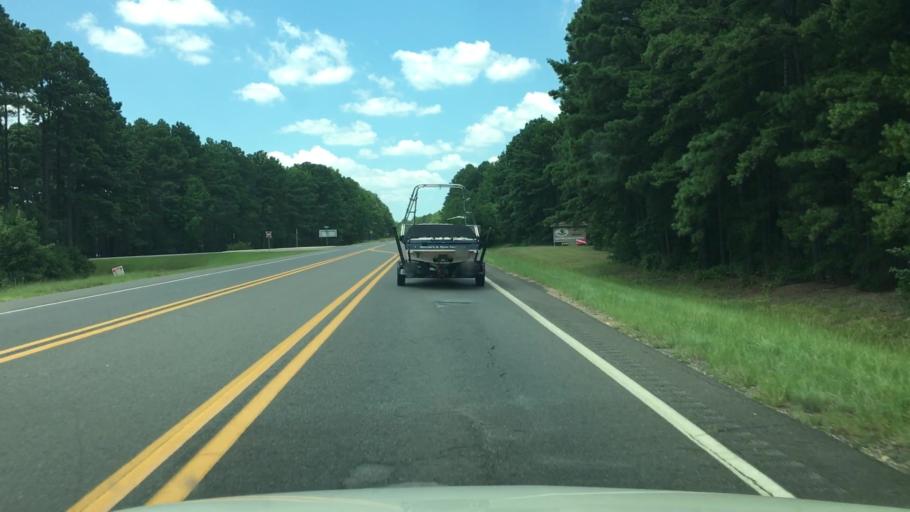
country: US
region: Arkansas
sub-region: Clark County
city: Arkadelphia
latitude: 34.2188
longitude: -93.0864
